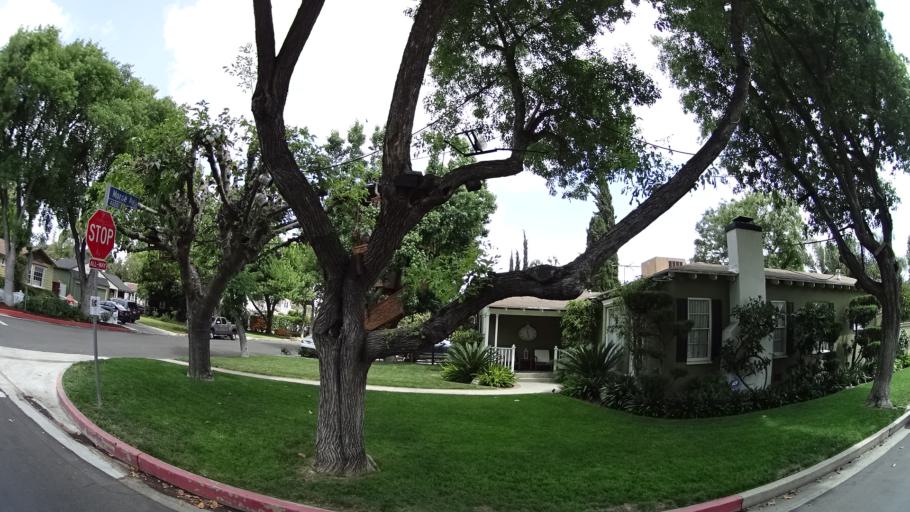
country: US
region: California
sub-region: Los Angeles County
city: Sherman Oaks
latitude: 34.1540
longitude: -118.4159
